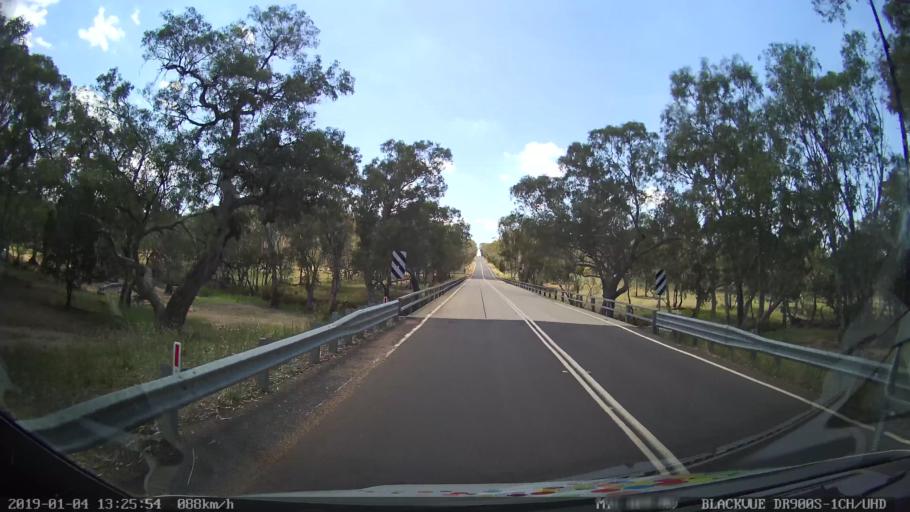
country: AU
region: New South Wales
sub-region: Parkes
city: Peak Hill
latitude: -32.6870
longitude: 148.5544
